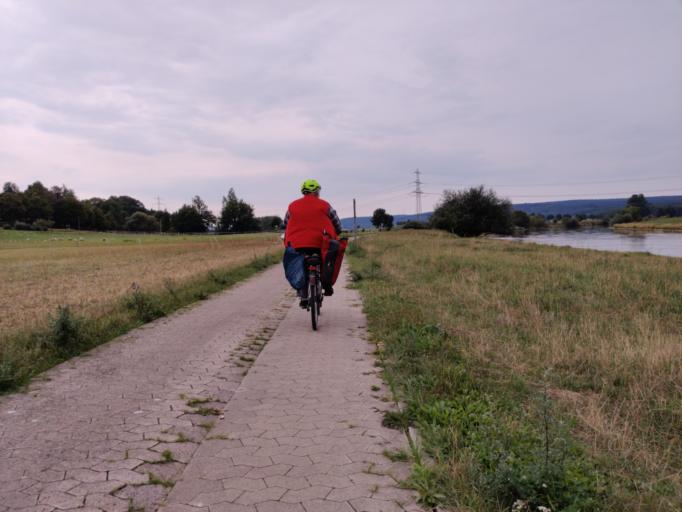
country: DE
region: Lower Saxony
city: Hehlen
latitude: 52.0296
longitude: 9.4303
